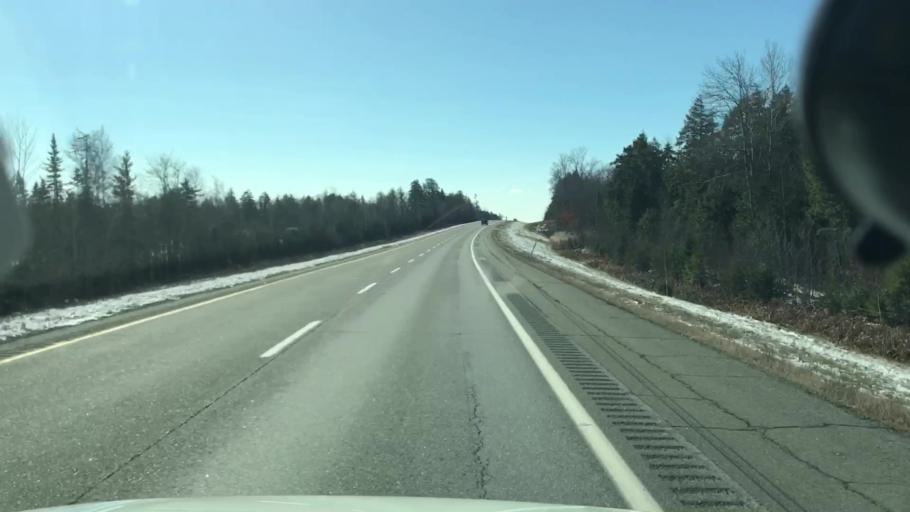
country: US
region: Maine
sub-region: Penobscot County
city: Howland
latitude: 45.2861
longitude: -68.6680
